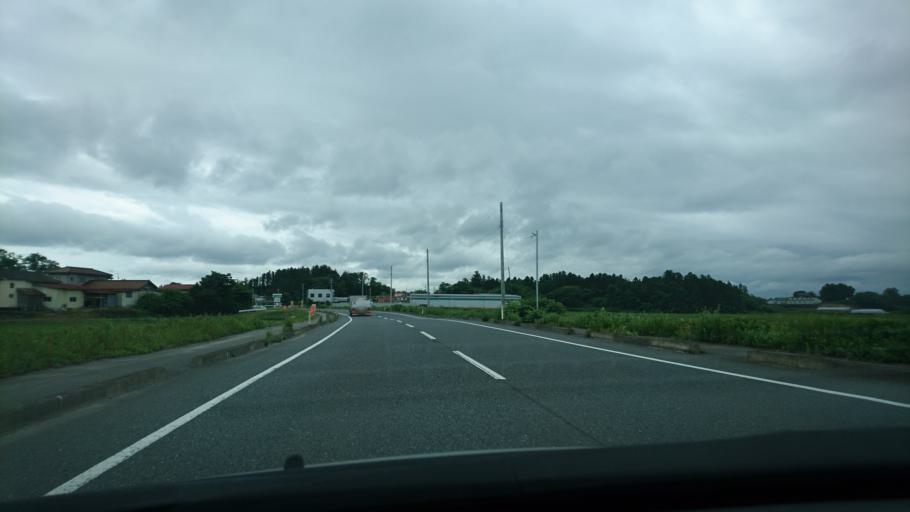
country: JP
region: Iwate
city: Ichinoseki
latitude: 38.7435
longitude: 141.2555
